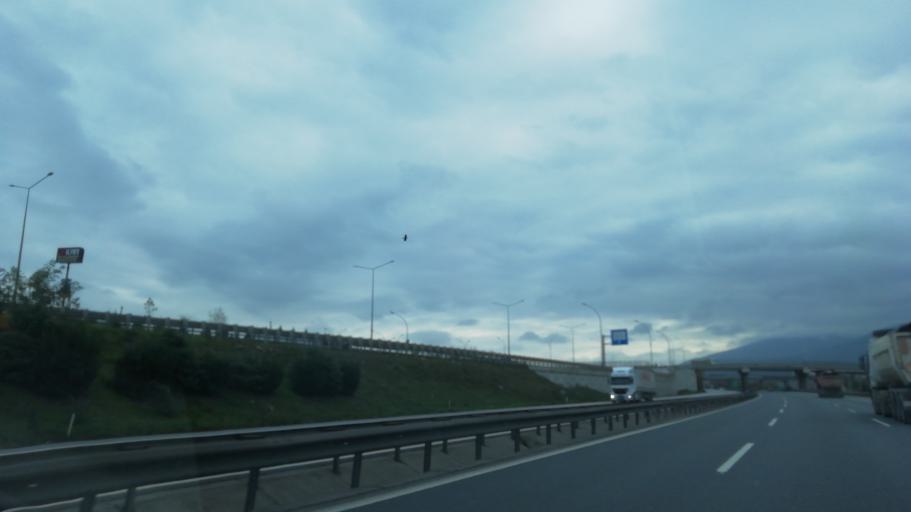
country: TR
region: Kocaeli
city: Derbent
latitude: 40.7334
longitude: 30.0540
